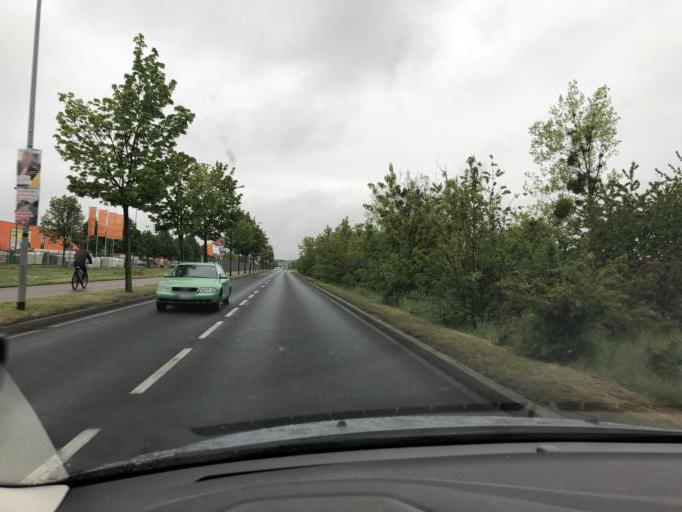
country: DE
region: Saxony-Anhalt
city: Dessau
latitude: 51.8208
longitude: 12.2157
